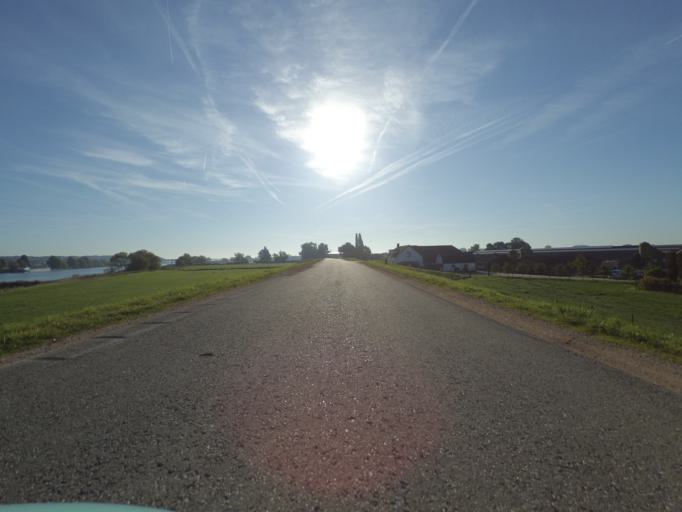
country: NL
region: Utrecht
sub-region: Gemeente Rhenen
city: Rhenen
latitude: 51.9540
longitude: 5.5575
